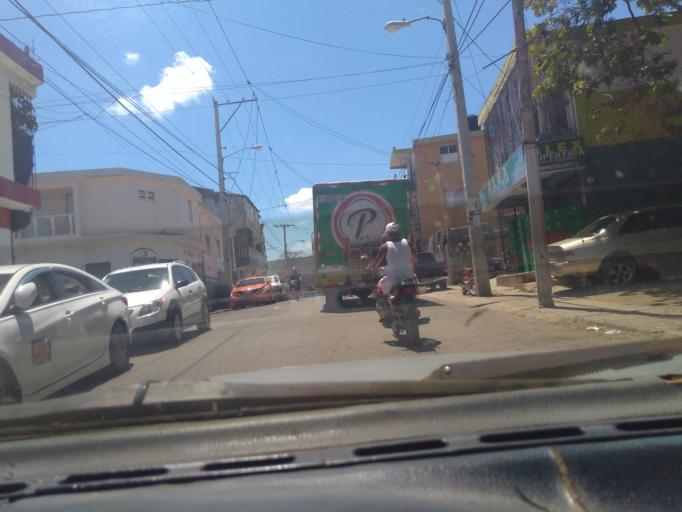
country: DO
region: Santiago
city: Palmar Arriba
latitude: 19.4849
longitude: -70.7432
